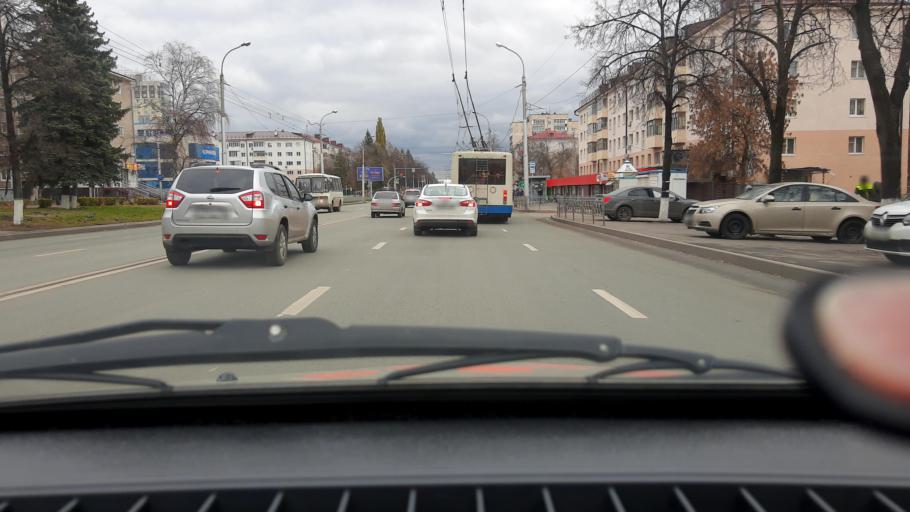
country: RU
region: Bashkortostan
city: Ufa
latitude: 54.8109
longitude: 56.0978
